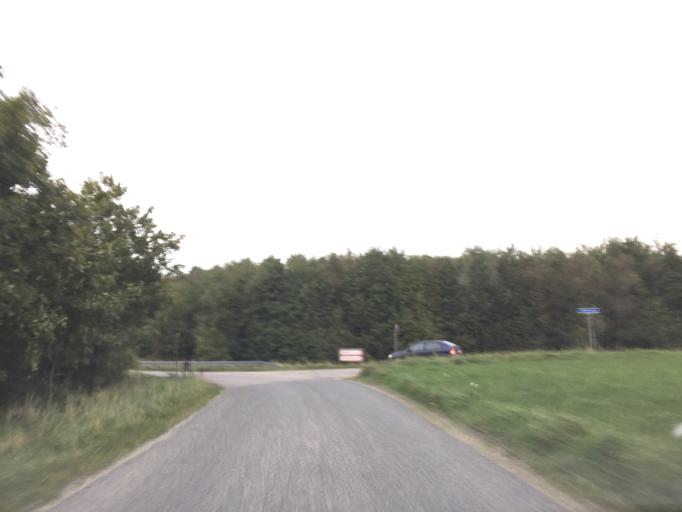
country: DK
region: Central Jutland
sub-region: Viborg Kommune
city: Bjerringbro
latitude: 56.2689
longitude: 9.6923
